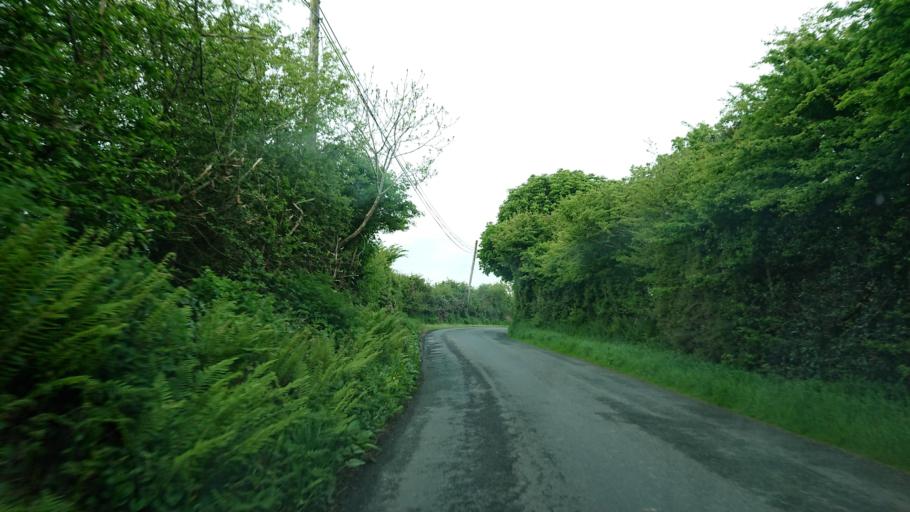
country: IE
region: Munster
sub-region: Waterford
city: Waterford
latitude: 52.2225
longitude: -7.0354
